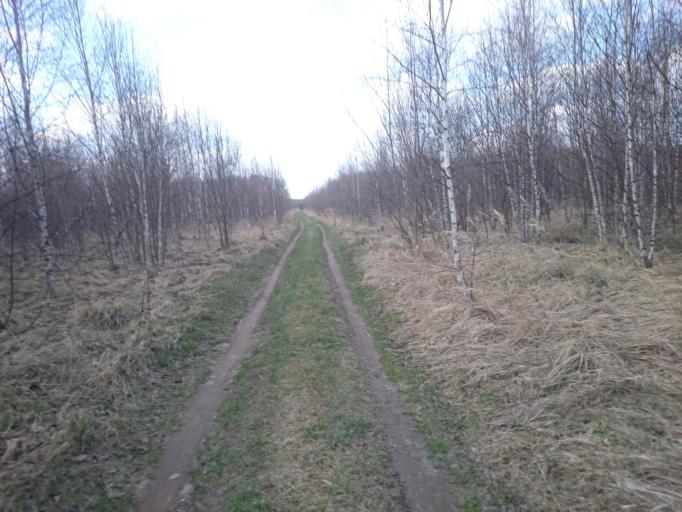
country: RU
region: Moskovskaya
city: Klin
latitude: 56.4006
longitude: 36.6814
